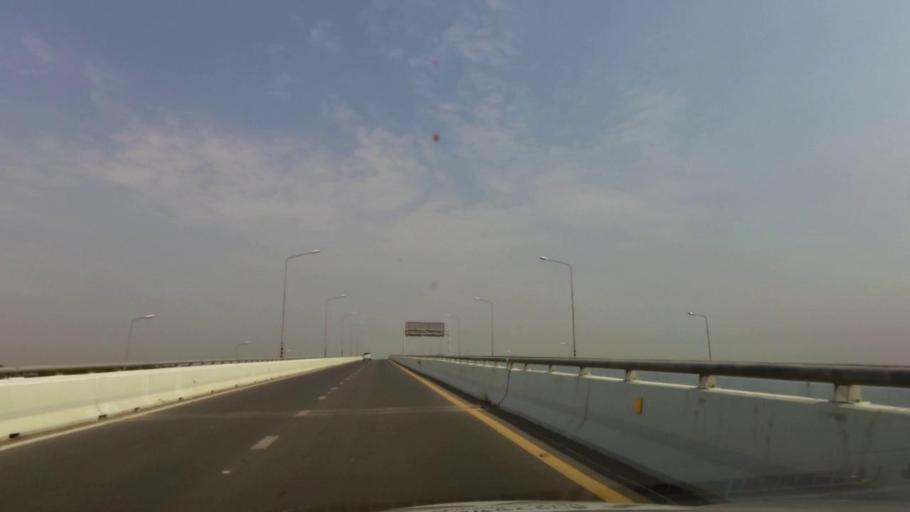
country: TH
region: Phra Nakhon Si Ayutthaya
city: Phra Nakhon Si Ayutthaya
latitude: 14.3305
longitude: 100.5812
